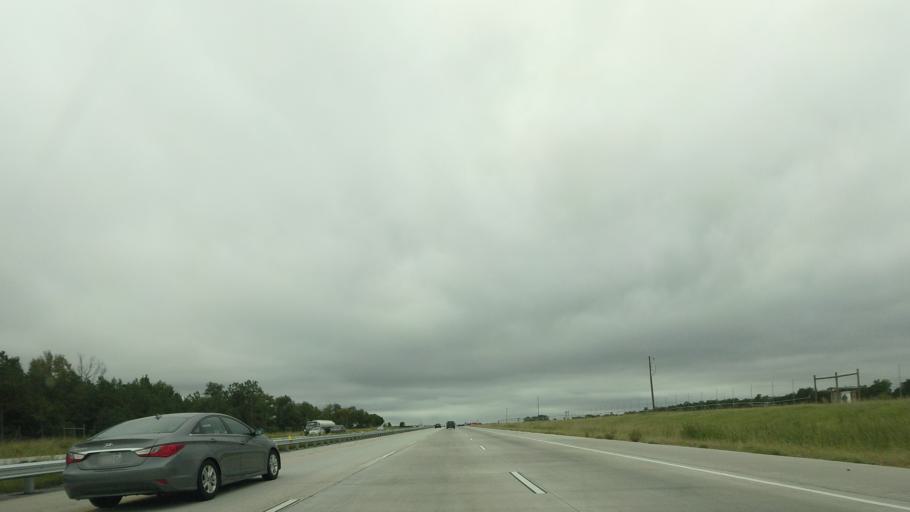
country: US
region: Georgia
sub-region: Dooly County
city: Vienna
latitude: 32.1605
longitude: -83.7546
